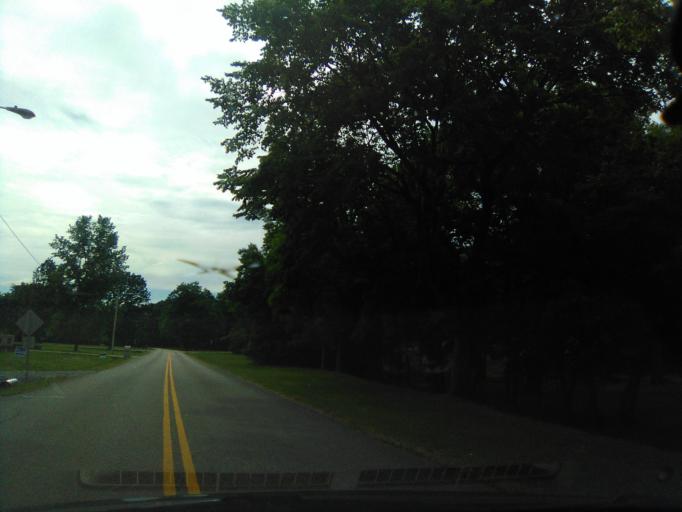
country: US
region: Tennessee
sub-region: Davidson County
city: Belle Meade
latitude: 36.1036
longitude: -86.8903
